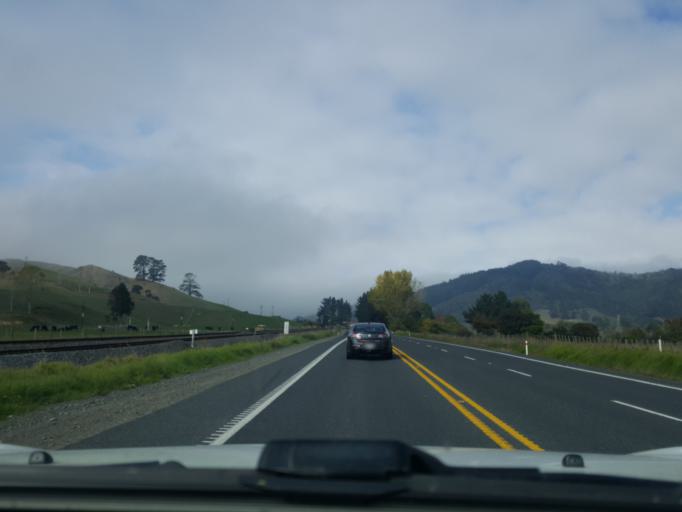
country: NZ
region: Waikato
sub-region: Waikato District
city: Ngaruawahia
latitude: -37.5945
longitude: 175.1607
